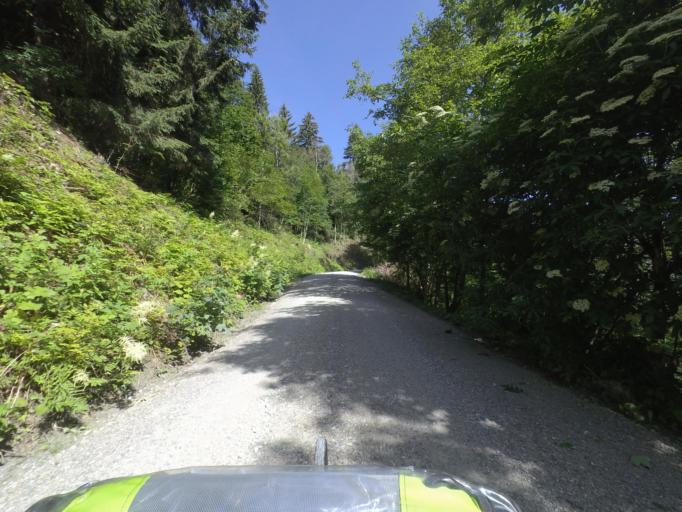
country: AT
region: Salzburg
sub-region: Politischer Bezirk Sankt Johann im Pongau
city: Dorfgastein
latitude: 47.2620
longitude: 13.0759
